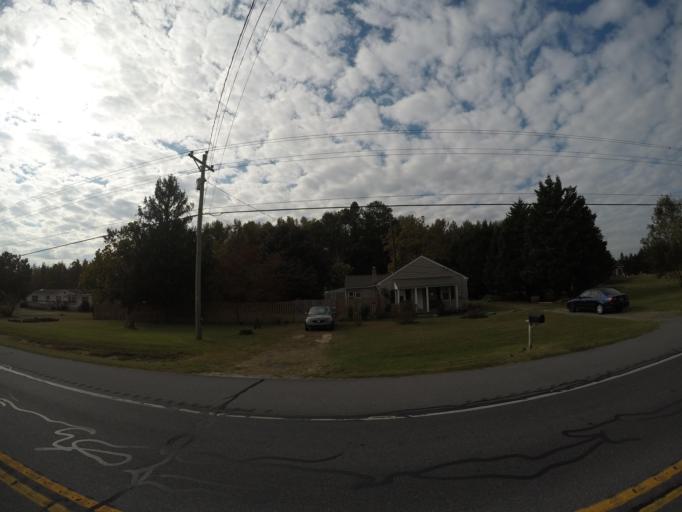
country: US
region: Delaware
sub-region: Sussex County
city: Bridgeville
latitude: 38.7054
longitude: -75.5134
